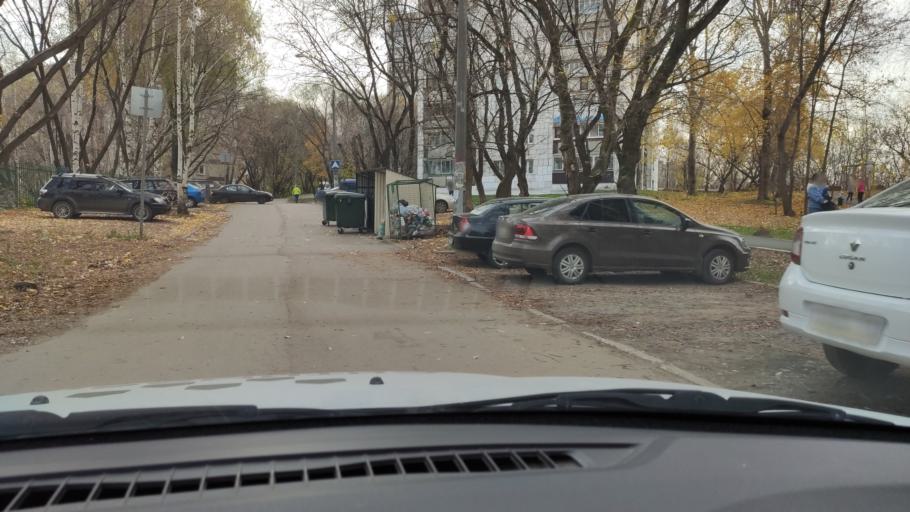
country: RU
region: Perm
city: Perm
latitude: 57.9823
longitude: 56.2315
